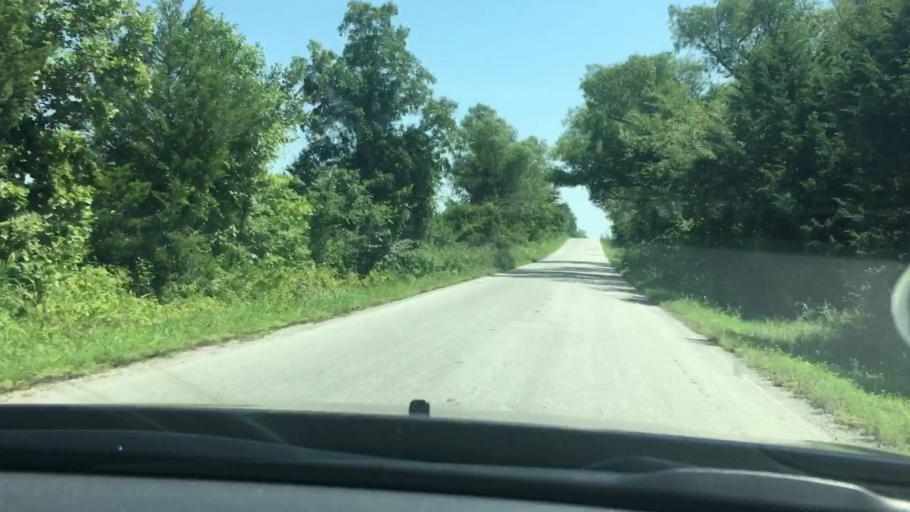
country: US
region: Oklahoma
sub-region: Bryan County
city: Durant
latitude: 34.2587
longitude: -96.3889
